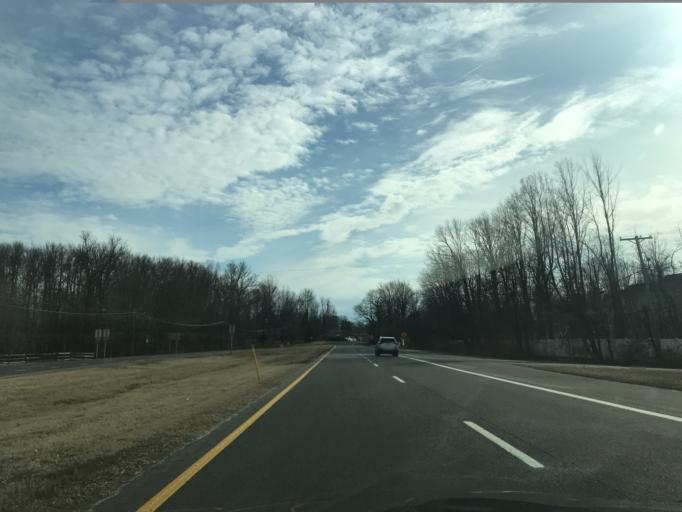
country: US
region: Maryland
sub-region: Prince George's County
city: Glenn Dale
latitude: 38.9608
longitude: -76.7977
